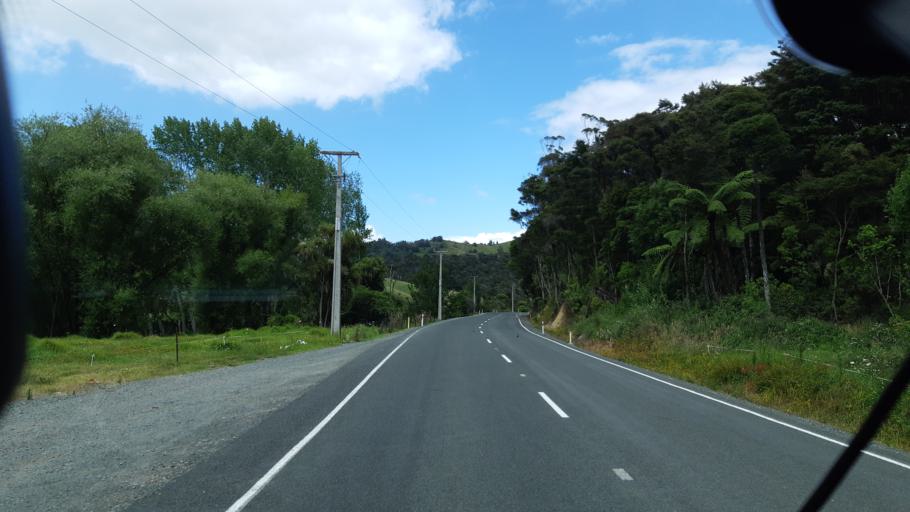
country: NZ
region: Northland
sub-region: Far North District
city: Taipa
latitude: -35.2407
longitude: 173.5406
